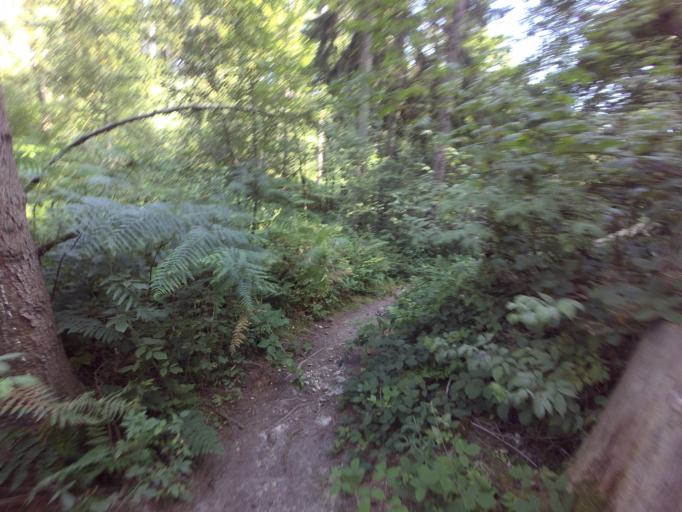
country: BE
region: Wallonia
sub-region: Province de Liege
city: Aubel
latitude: 50.7574
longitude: 5.8907
